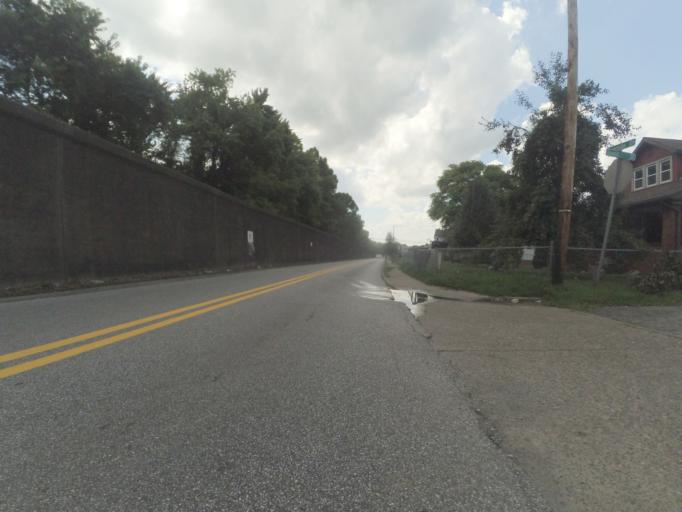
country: US
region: West Virginia
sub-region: Cabell County
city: Pea Ridge
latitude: 38.4123
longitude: -82.3785
